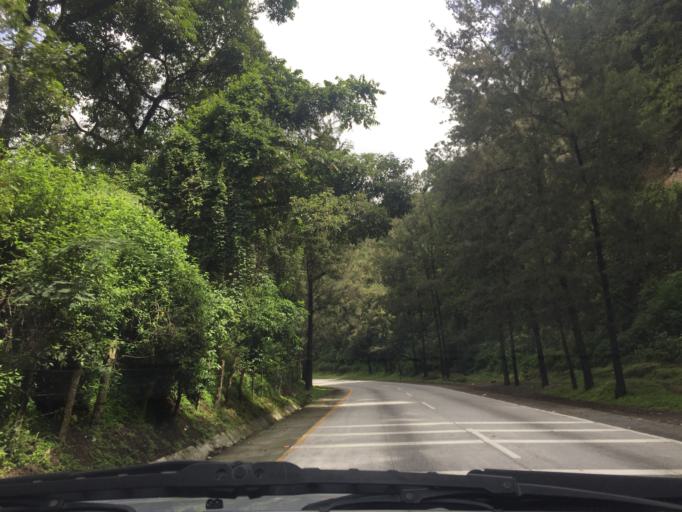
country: GT
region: Sacatepequez
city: Santa Lucia Milpas Altas
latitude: 14.5603
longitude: -90.6981
